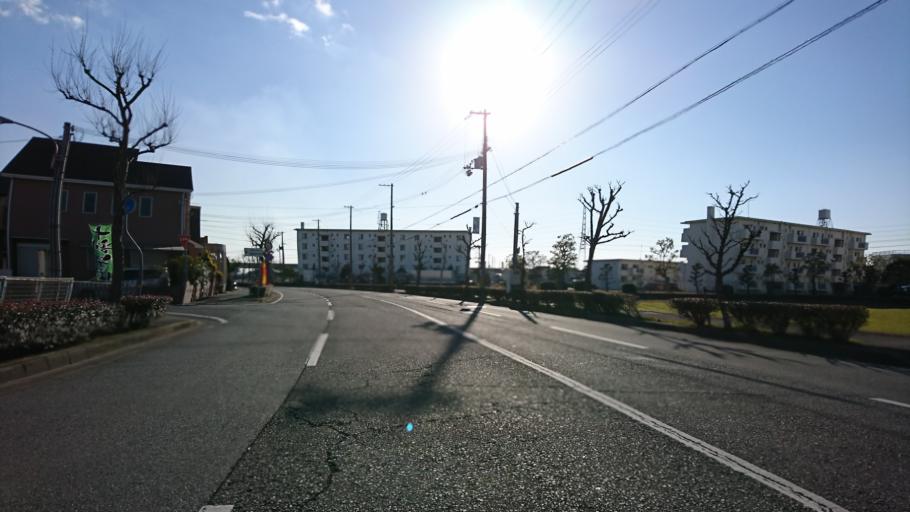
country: JP
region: Hyogo
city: Kakogawacho-honmachi
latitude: 34.7405
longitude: 134.8427
